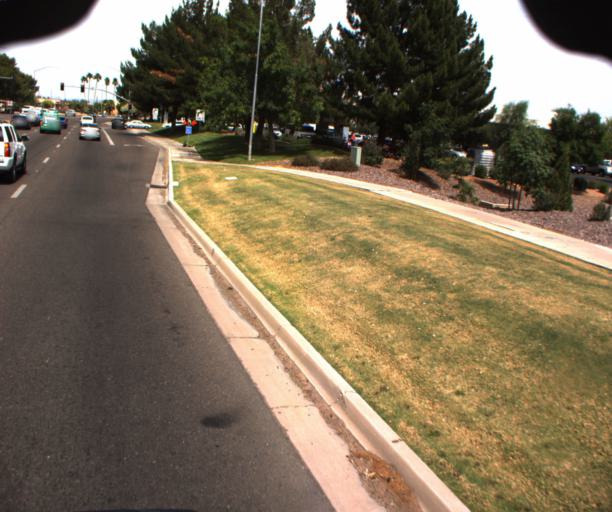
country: US
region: Arizona
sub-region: Maricopa County
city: San Carlos
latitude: 33.3748
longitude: -111.8422
